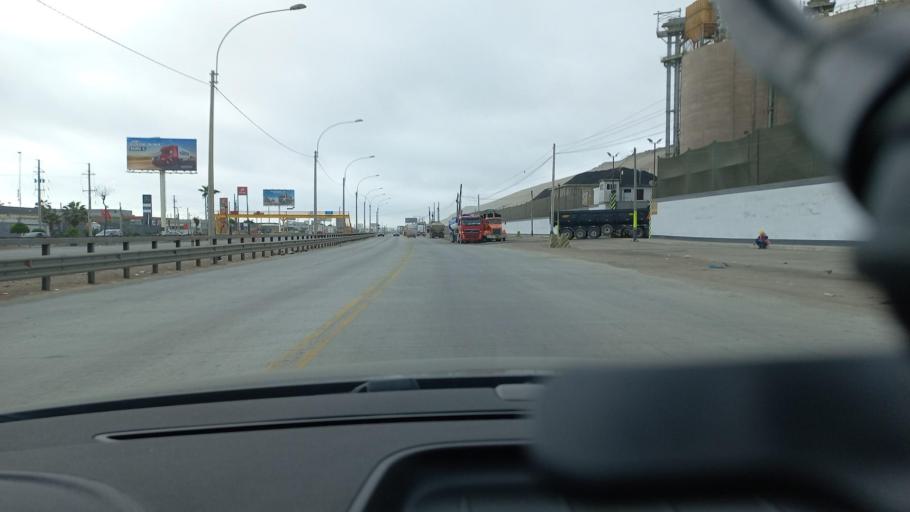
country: PE
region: Lima
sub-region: Lima
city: Surco
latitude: -12.2471
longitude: -76.9344
